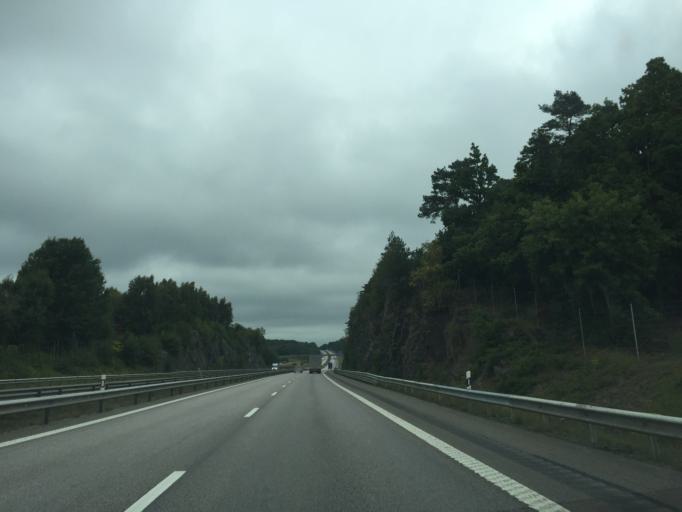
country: SE
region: Halland
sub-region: Kungsbacka Kommun
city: Fjaeras kyrkby
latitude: 57.4121
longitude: 12.1721
